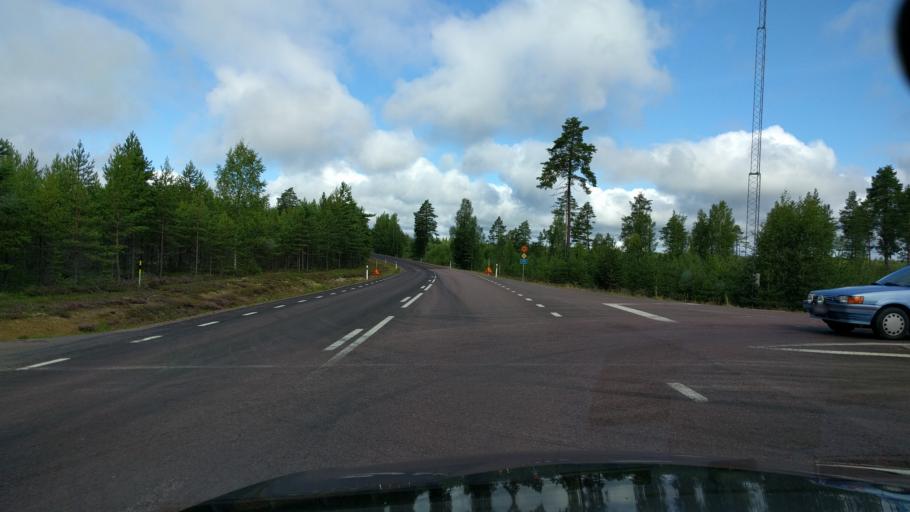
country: SE
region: Dalarna
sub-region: Mora Kommun
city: Mora
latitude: 61.0464
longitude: 14.4960
